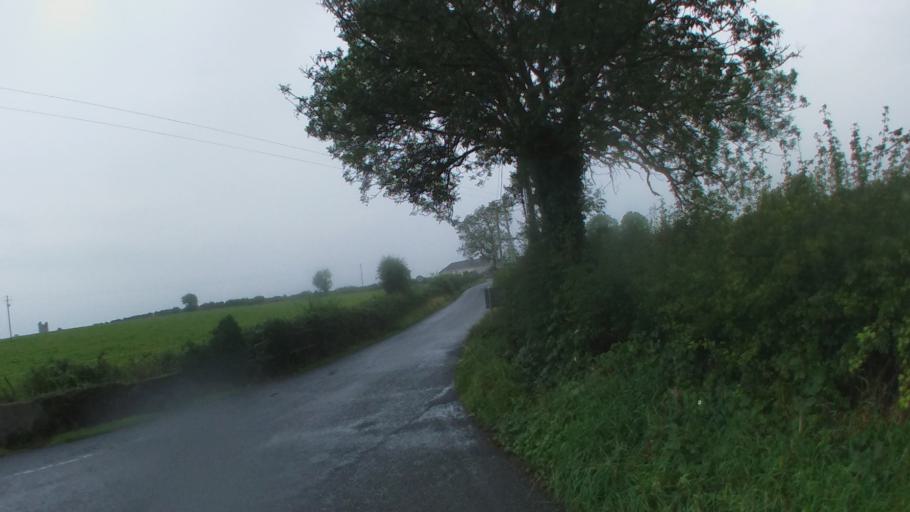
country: IE
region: Leinster
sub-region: Kilkenny
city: Callan
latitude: 52.5478
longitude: -7.3122
